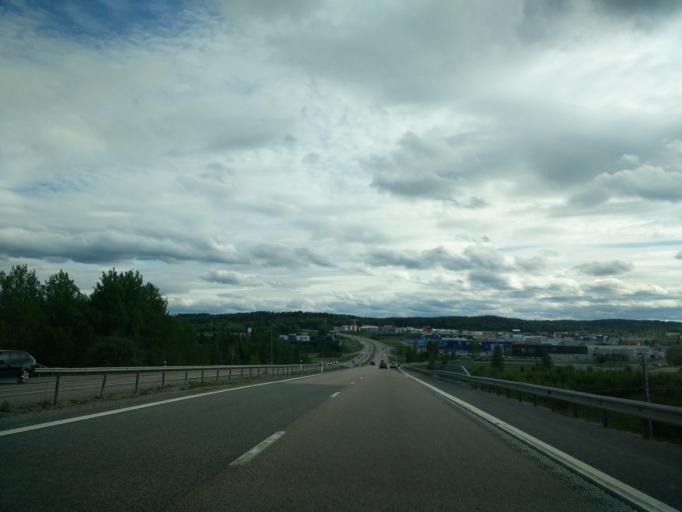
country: SE
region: Vaesternorrland
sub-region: Sundsvalls Kommun
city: Sundsbruk
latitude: 62.4510
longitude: 17.3432
